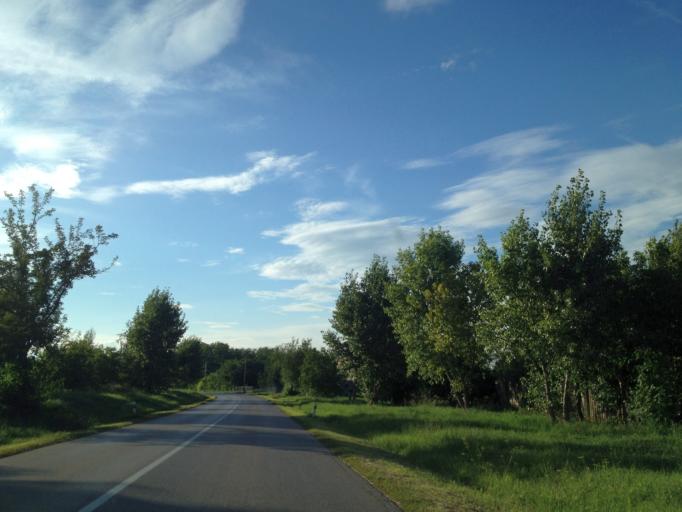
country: SK
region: Nitriansky
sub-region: Okres Komarno
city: Hurbanovo
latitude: 47.8620
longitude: 18.2728
